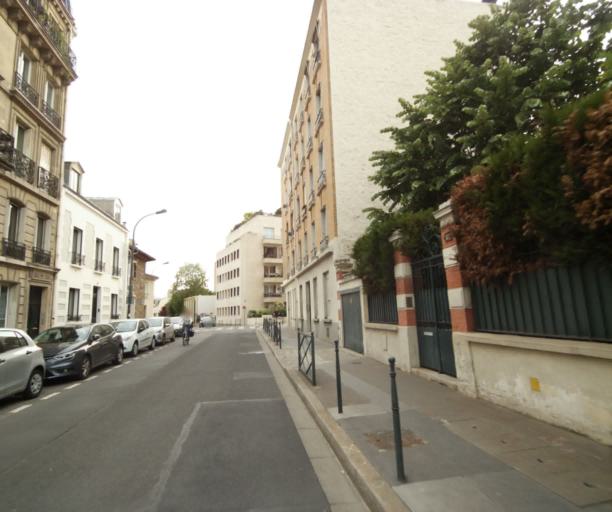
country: FR
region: Ile-de-France
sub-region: Departement des Hauts-de-Seine
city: Asnieres-sur-Seine
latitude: 48.9096
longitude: 2.2924
